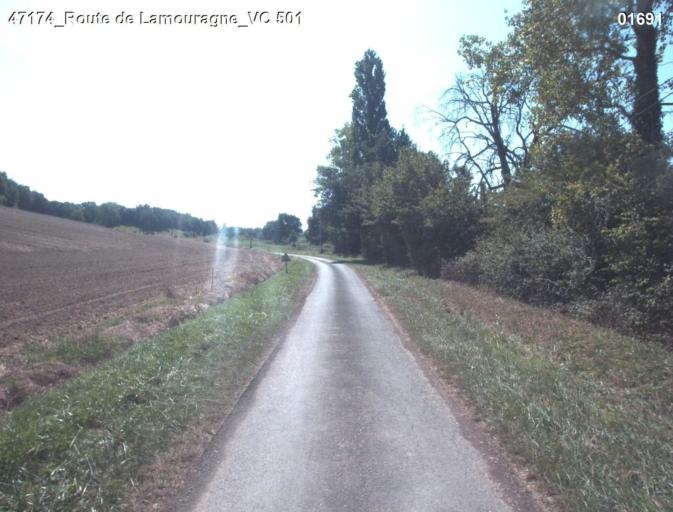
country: FR
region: Midi-Pyrenees
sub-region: Departement du Gers
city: Condom
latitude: 44.0335
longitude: 0.3917
